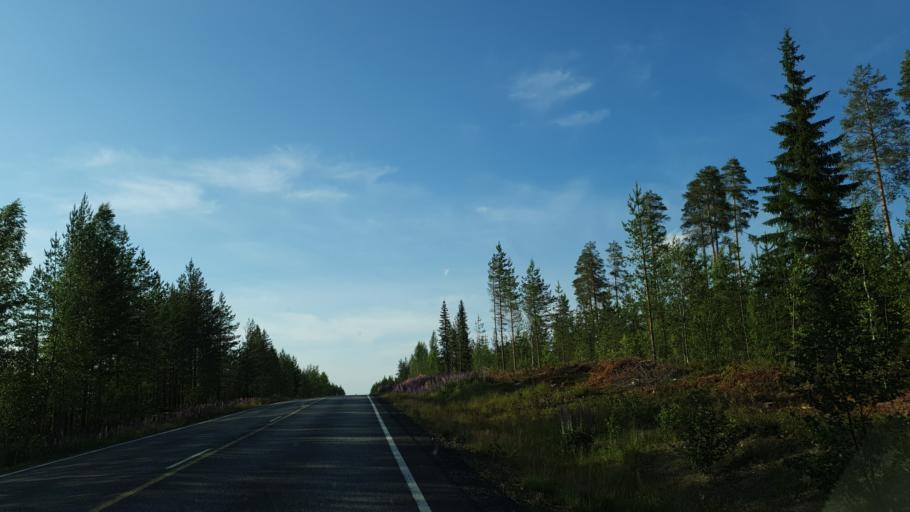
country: FI
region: Kainuu
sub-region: Kehys-Kainuu
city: Kuhmo
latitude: 64.0838
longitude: 29.4843
